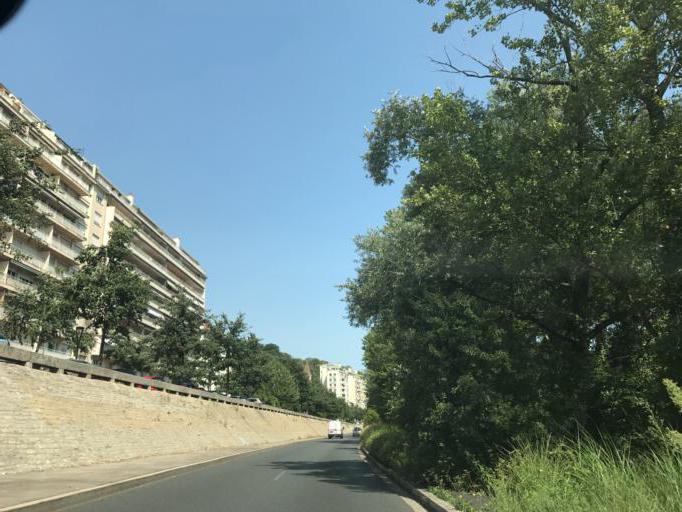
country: FR
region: Rhone-Alpes
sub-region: Departement du Rhone
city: Caluire-et-Cuire
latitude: 45.7827
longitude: 4.8442
